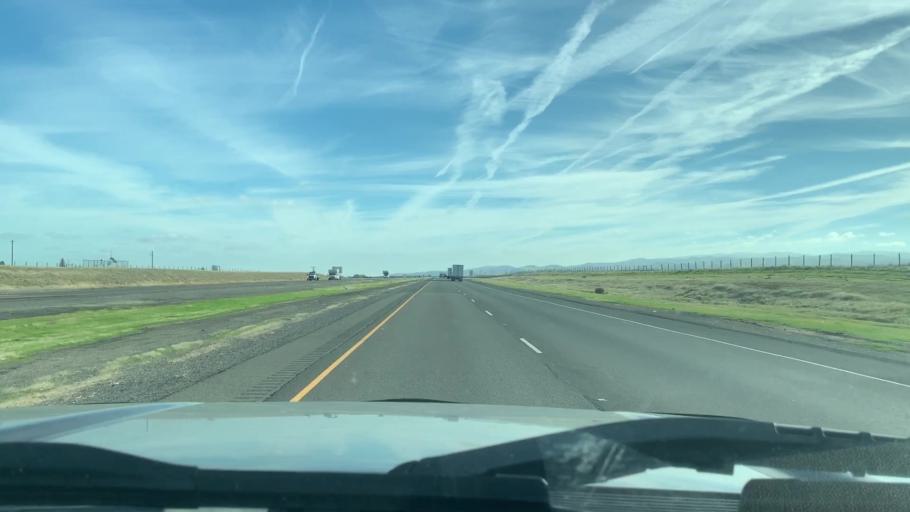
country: US
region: California
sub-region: Fresno County
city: Mendota
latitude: 36.6354
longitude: -120.6198
